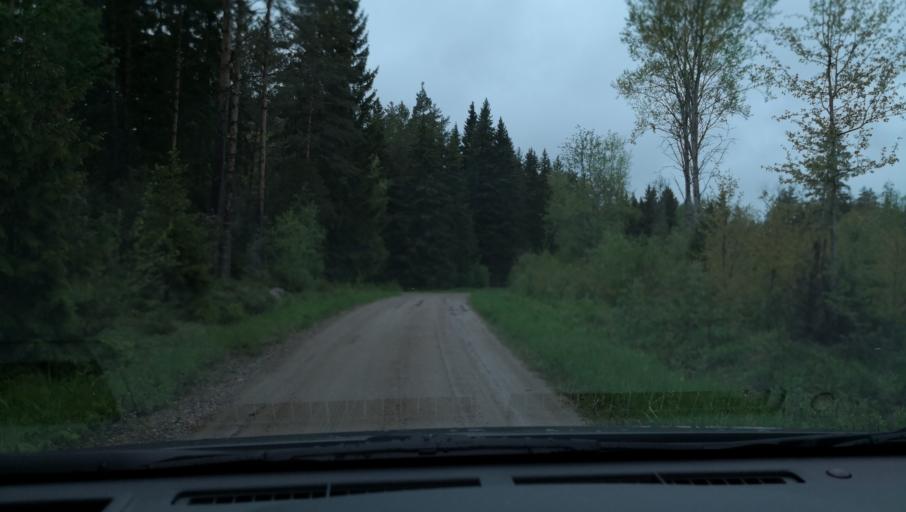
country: SE
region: Uppsala
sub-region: Enkopings Kommun
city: Orsundsbro
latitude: 59.9150
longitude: 17.3489
